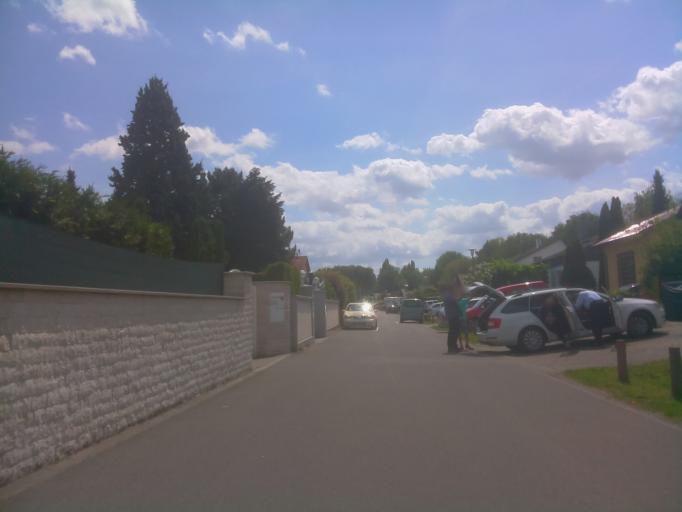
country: DE
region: Rheinland-Pfalz
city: Otterstadt
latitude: 49.3584
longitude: 8.4468
